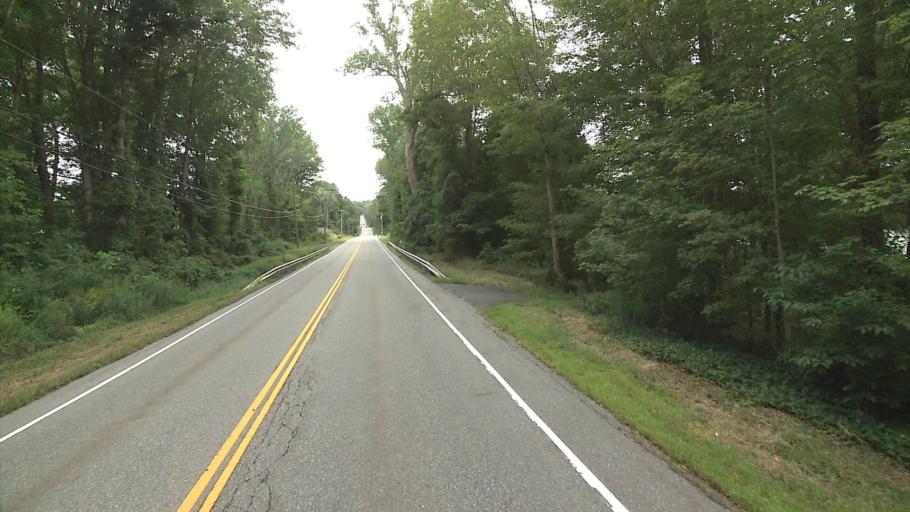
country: US
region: Connecticut
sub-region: Hartford County
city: Terramuggus
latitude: 41.7004
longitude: -72.4356
